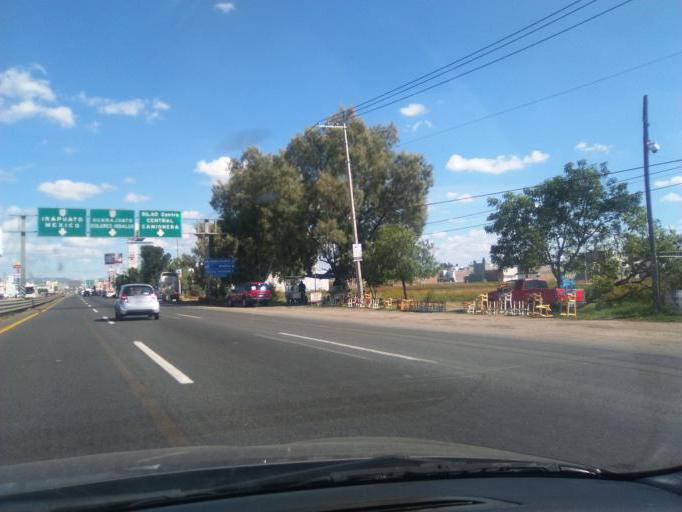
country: MX
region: Guanajuato
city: Silao
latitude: 20.9558
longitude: -101.4351
